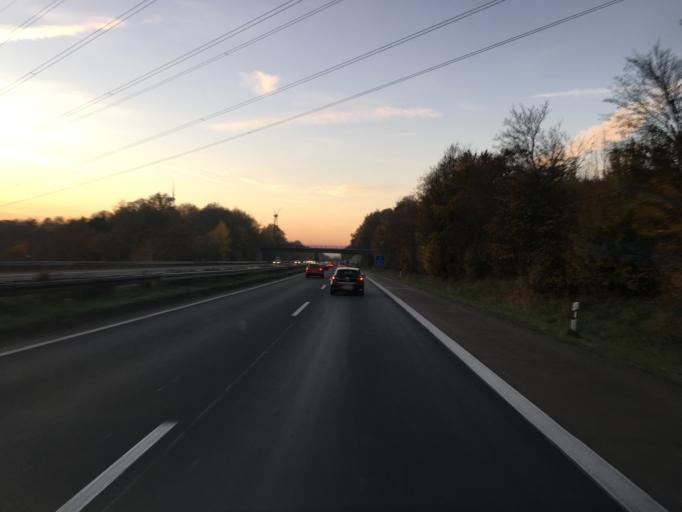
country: DE
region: North Rhine-Westphalia
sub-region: Regierungsbezirk Arnsberg
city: Nachrodt-Wiblingwerde
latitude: 51.3175
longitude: 7.5479
